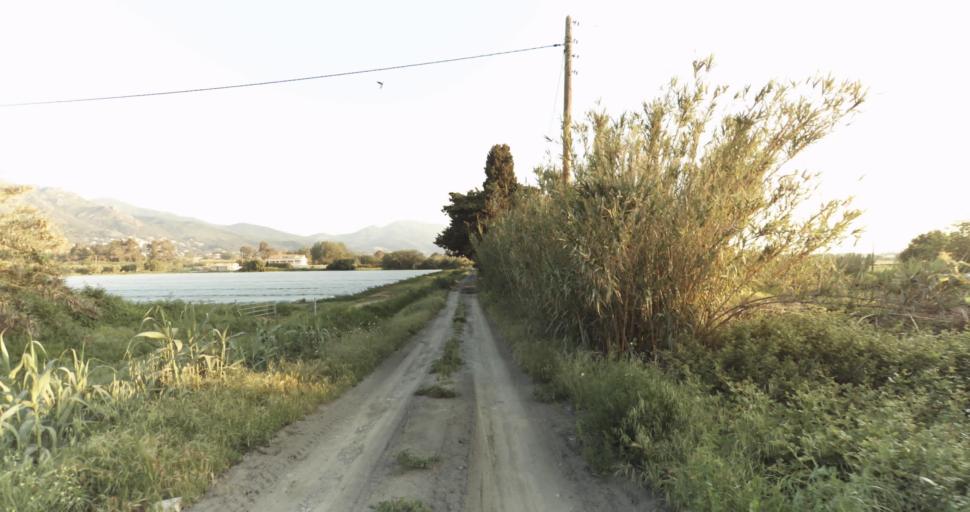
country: FR
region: Corsica
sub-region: Departement de la Haute-Corse
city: Biguglia
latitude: 42.6105
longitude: 9.4474
